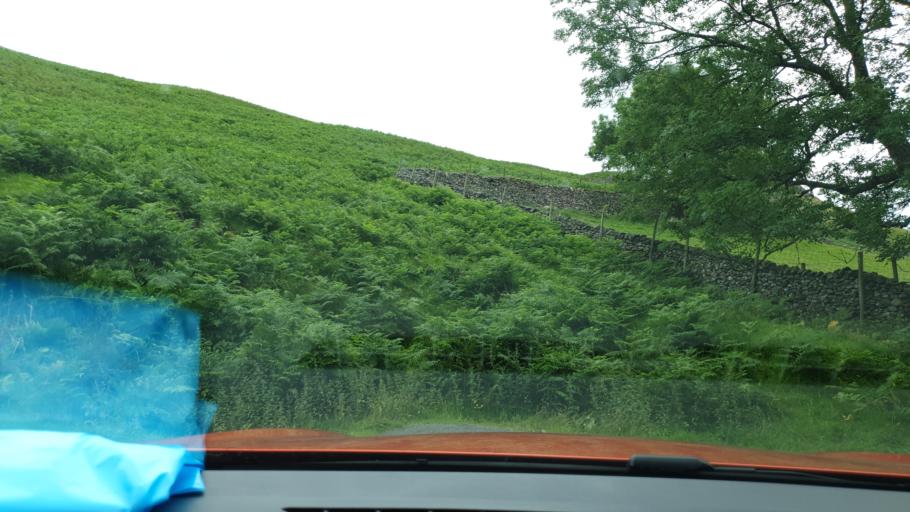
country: GB
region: England
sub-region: Cumbria
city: Ambleside
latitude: 54.5611
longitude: -2.8853
